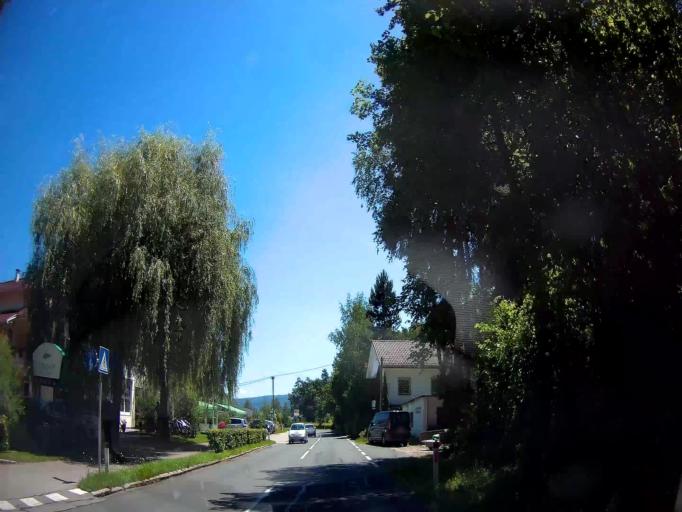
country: AT
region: Carinthia
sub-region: Politischer Bezirk Klagenfurt Land
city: Kottmannsdorf
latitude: 46.6070
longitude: 14.2523
